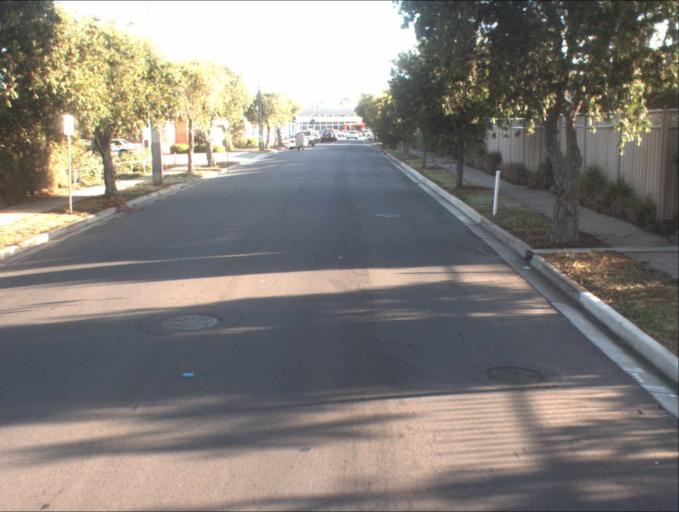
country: AU
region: South Australia
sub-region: Port Adelaide Enfield
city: Gilles Plains
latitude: -34.8617
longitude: 138.6521
